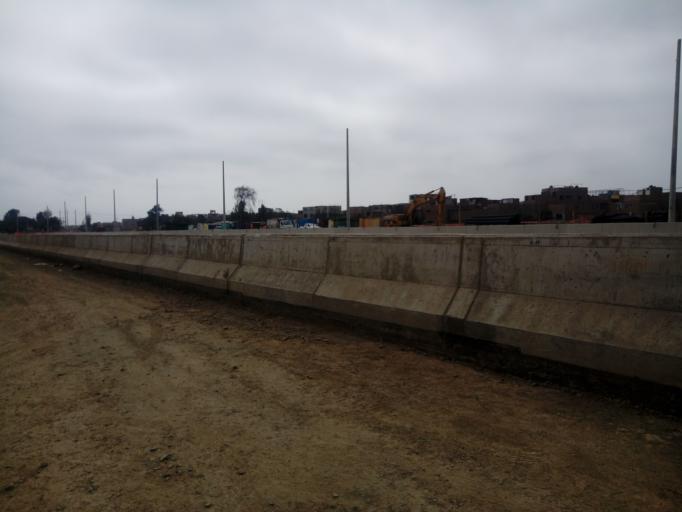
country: PE
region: Callao
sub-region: Callao
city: Callao
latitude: -12.0362
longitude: -77.0788
